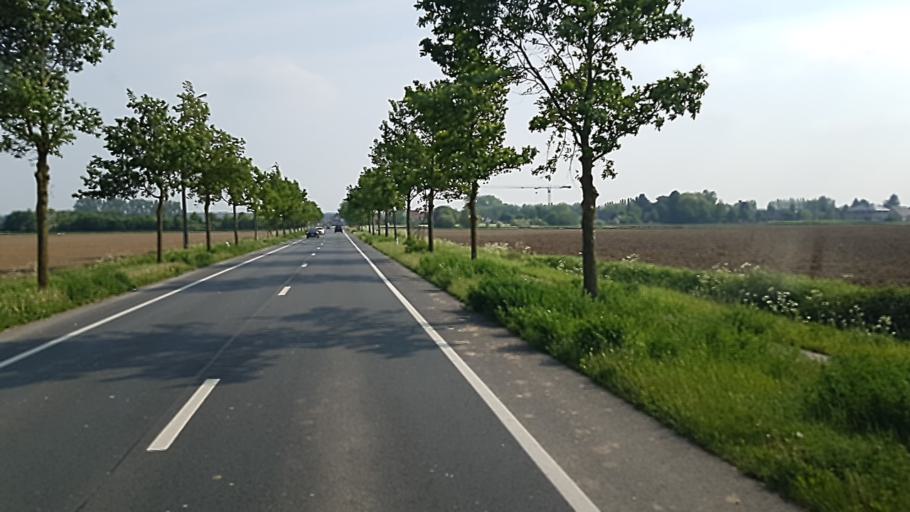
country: BE
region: Wallonia
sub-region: Province du Hainaut
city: Pecq
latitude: 50.7340
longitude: 3.3290
